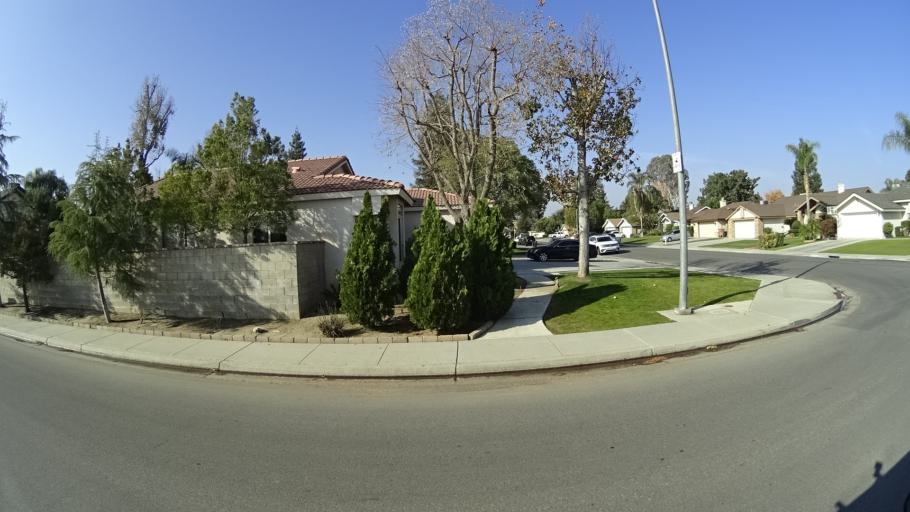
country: US
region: California
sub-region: Kern County
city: Greenacres
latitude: 35.3700
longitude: -119.1056
